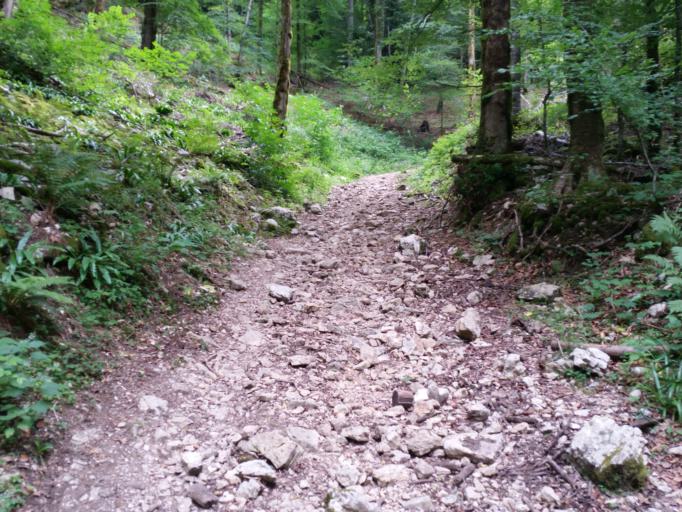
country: FR
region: Franche-Comte
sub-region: Departement du Jura
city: Salins-les-Bains
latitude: 46.9680
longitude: 5.9971
